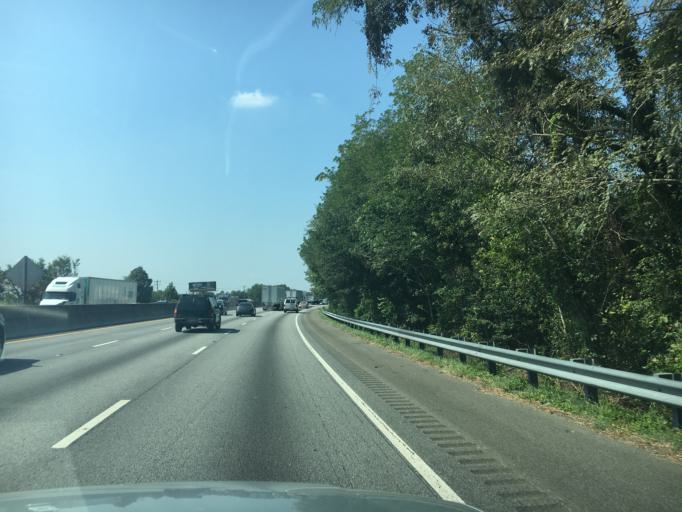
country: US
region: South Carolina
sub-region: Greenville County
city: Mauldin
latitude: 34.8039
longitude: -82.3517
